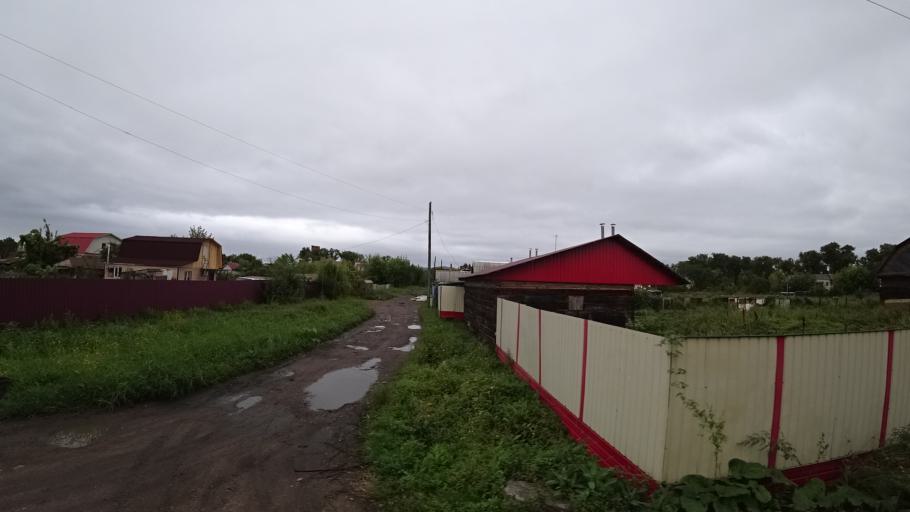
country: RU
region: Primorskiy
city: Chernigovka
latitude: 44.3365
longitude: 132.5349
